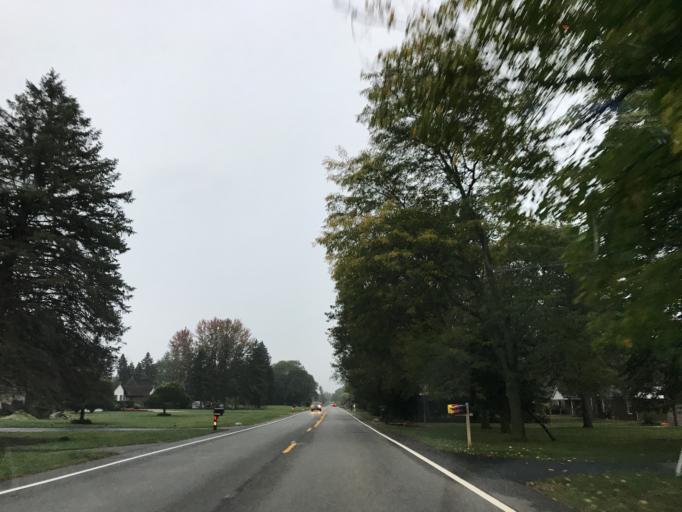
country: US
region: Michigan
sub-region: Oakland County
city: Farmington
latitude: 42.4623
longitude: -83.3178
